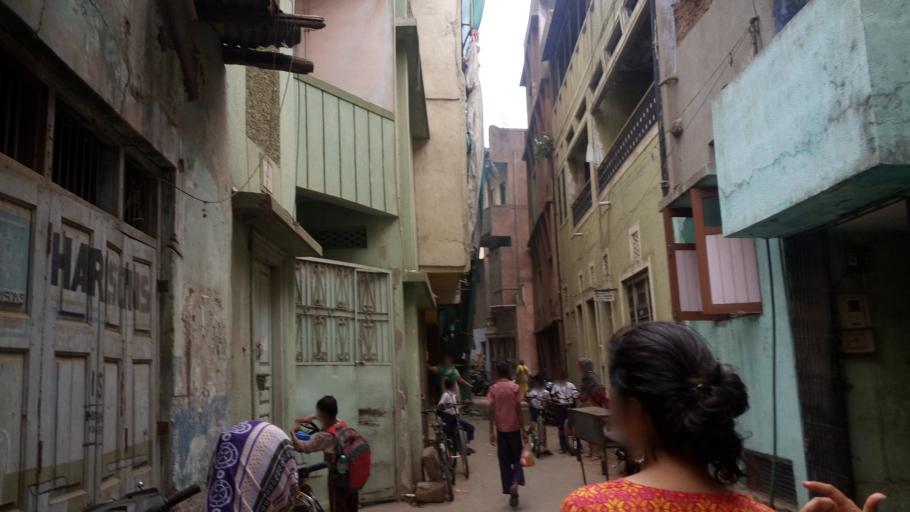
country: IN
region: Gujarat
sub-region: Ahmadabad
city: Ahmedabad
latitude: 23.0139
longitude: 72.5815
